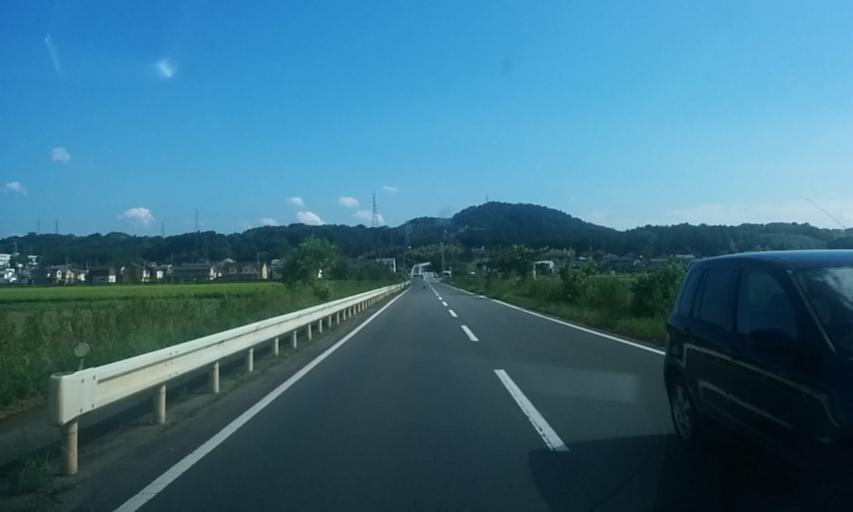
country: JP
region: Kyoto
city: Fukuchiyama
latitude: 35.3039
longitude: 135.1706
